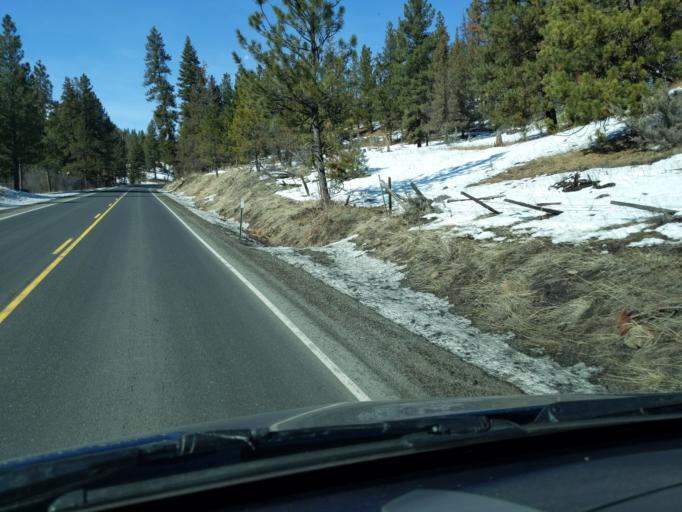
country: US
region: Oregon
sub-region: Grant County
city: John Day
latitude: 44.8926
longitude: -119.0130
